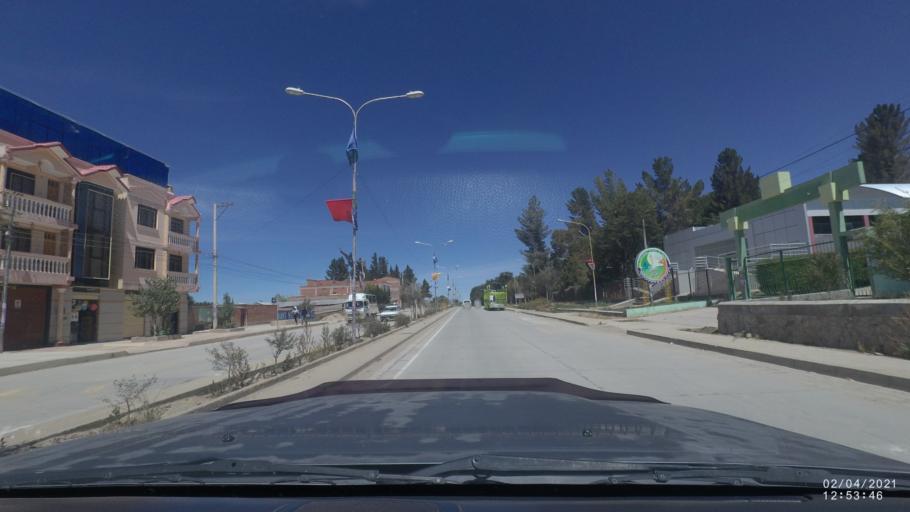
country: BO
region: Oruro
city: Oruro
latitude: -17.9939
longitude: -67.1354
